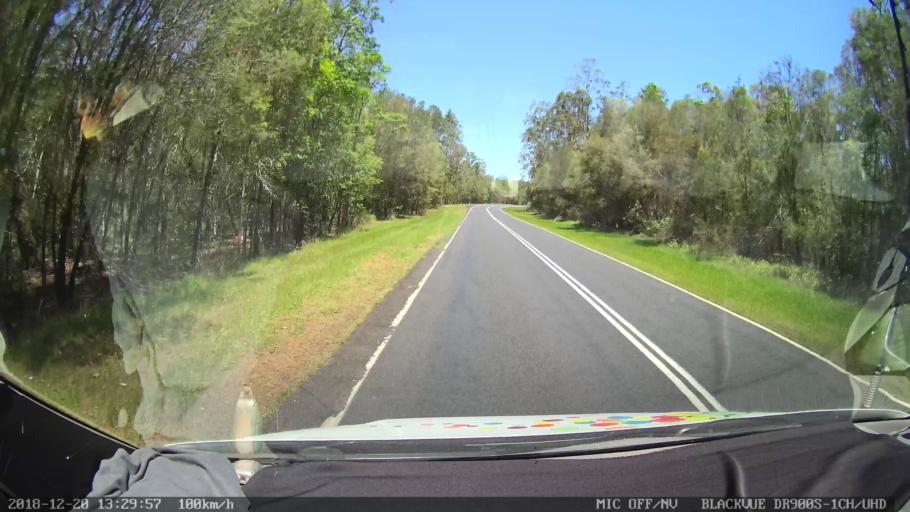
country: AU
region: New South Wales
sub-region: Clarence Valley
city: Gordon
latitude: -29.1967
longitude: 152.9918
